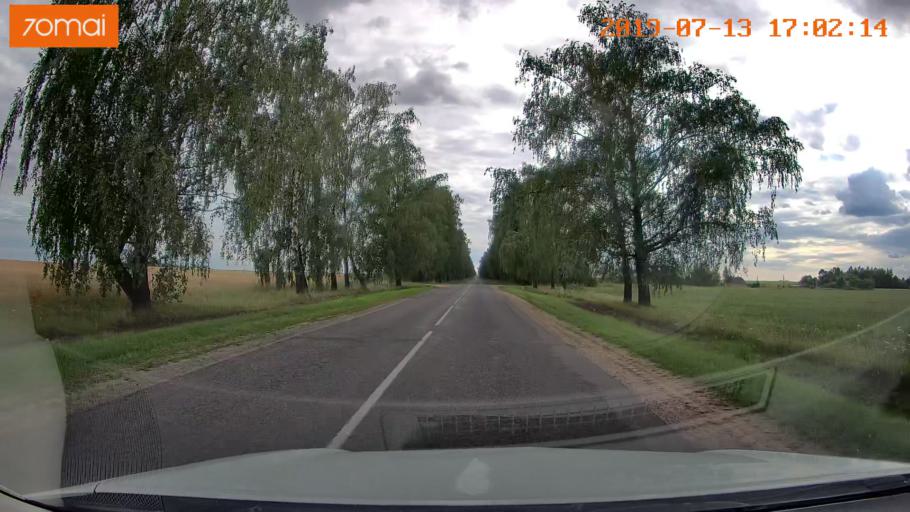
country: BY
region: Mogilev
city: Kirawsk
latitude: 53.2880
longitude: 29.3889
